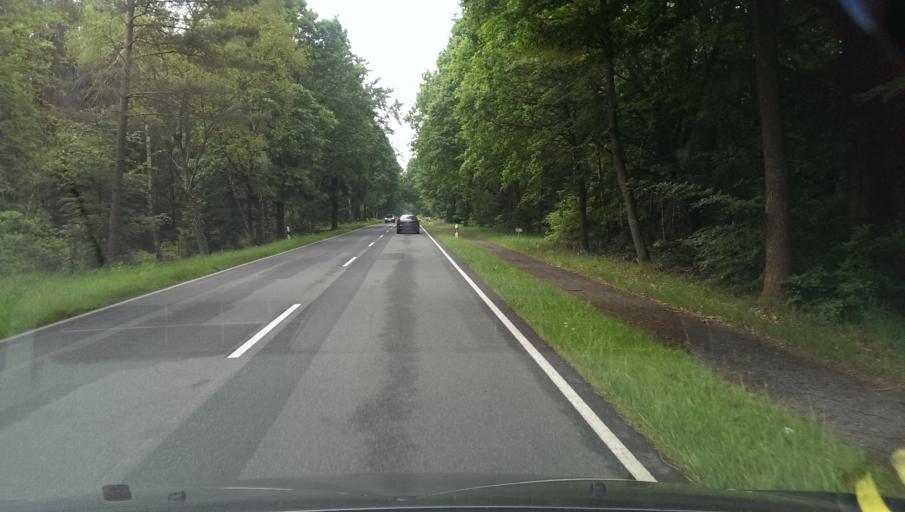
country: DE
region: Lower Saxony
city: Unterluss
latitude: 52.8132
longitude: 10.3497
